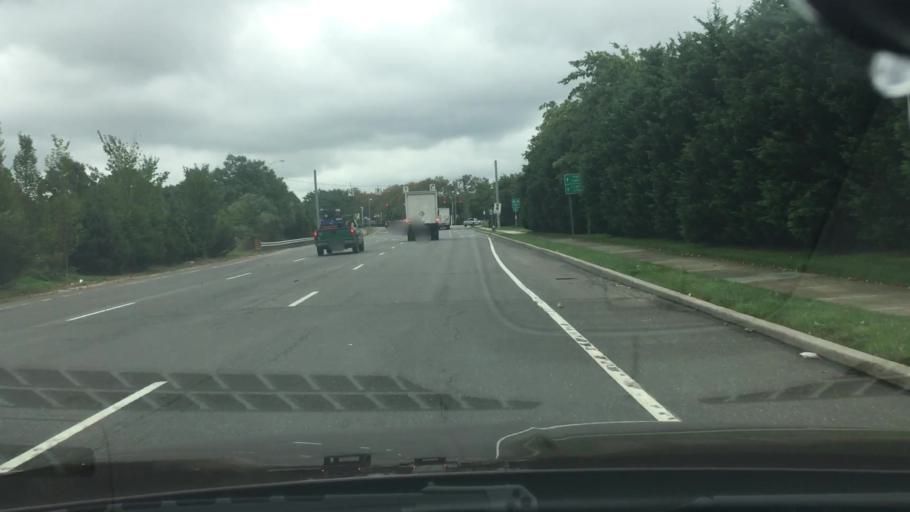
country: US
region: New York
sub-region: Suffolk County
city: Melville
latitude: 40.7794
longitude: -73.4221
